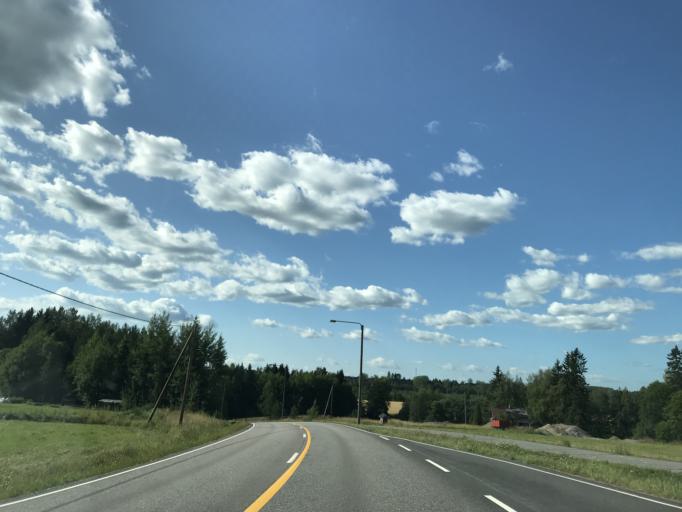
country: FI
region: Uusimaa
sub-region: Helsinki
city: Nurmijaervi
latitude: 60.4321
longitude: 24.8533
